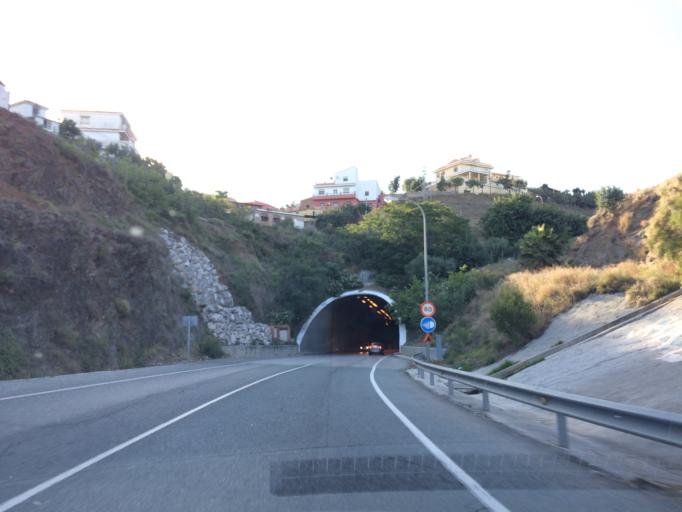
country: ES
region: Andalusia
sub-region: Provincia de Malaga
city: Malaga
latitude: 36.7404
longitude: -4.4114
